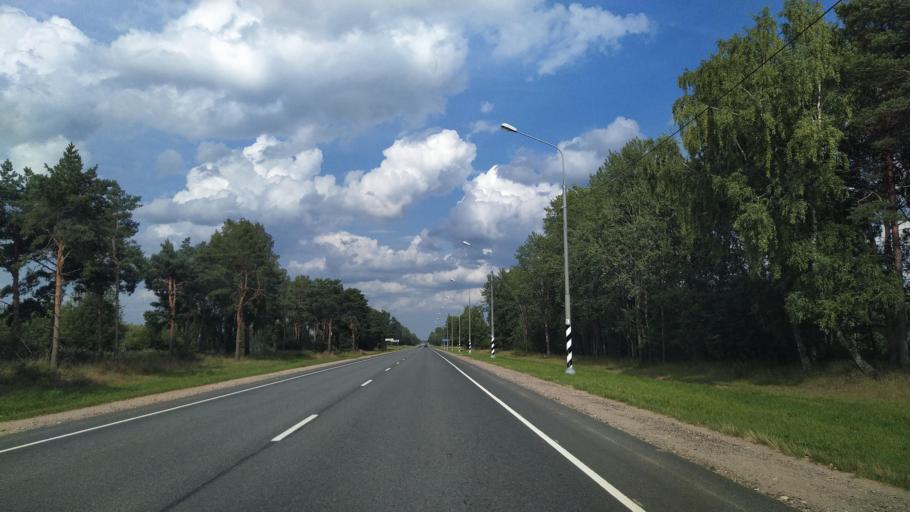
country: RU
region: Novgorod
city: Shimsk
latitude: 58.1807
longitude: 30.5387
